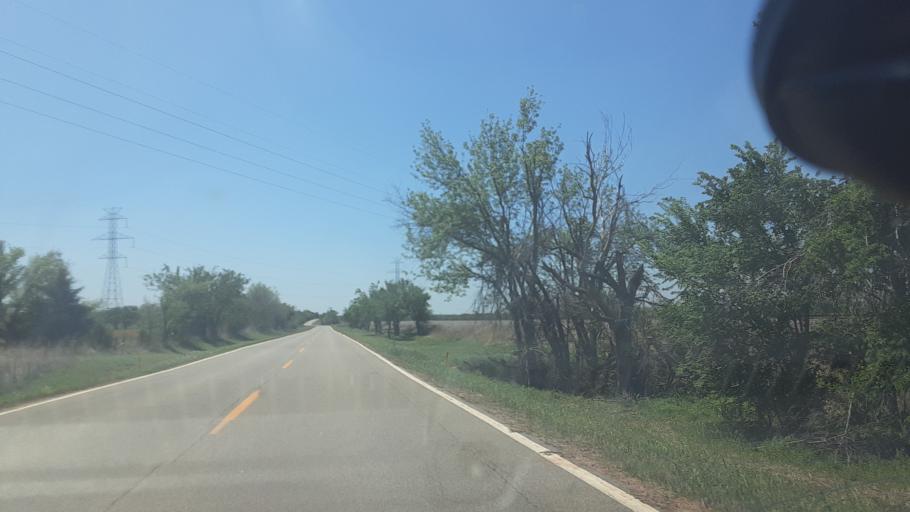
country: US
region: Oklahoma
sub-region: Logan County
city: Langston
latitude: 36.0979
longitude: -97.3944
